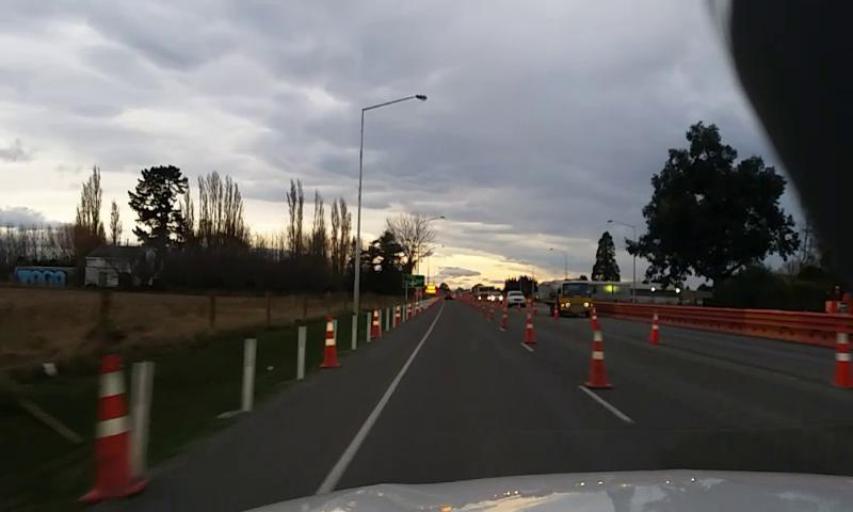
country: NZ
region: Canterbury
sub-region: Christchurch City
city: Christchurch
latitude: -43.4817
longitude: 172.5551
